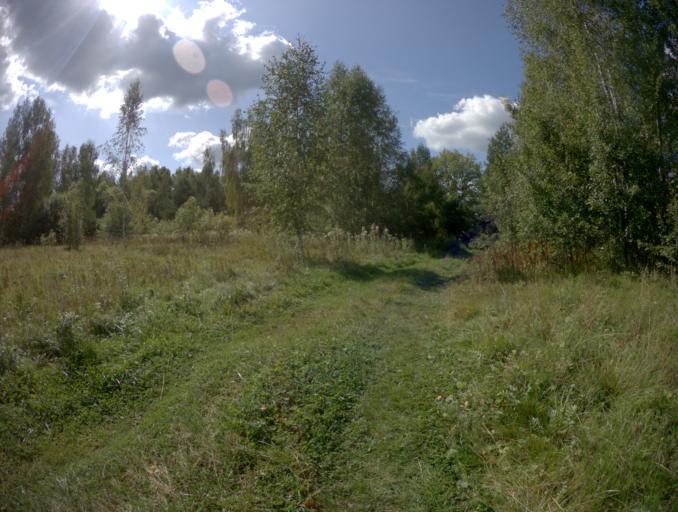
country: RU
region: Vladimir
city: Petushki
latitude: 55.8546
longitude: 39.3561
